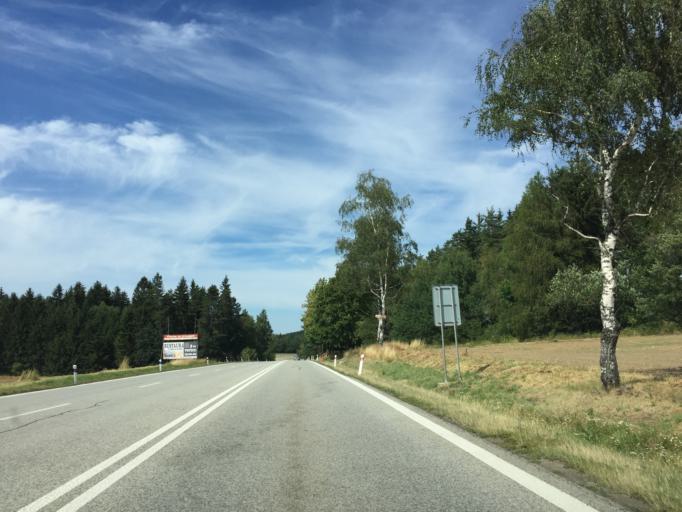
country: CZ
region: Central Bohemia
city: Votice
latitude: 49.6038
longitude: 14.6600
